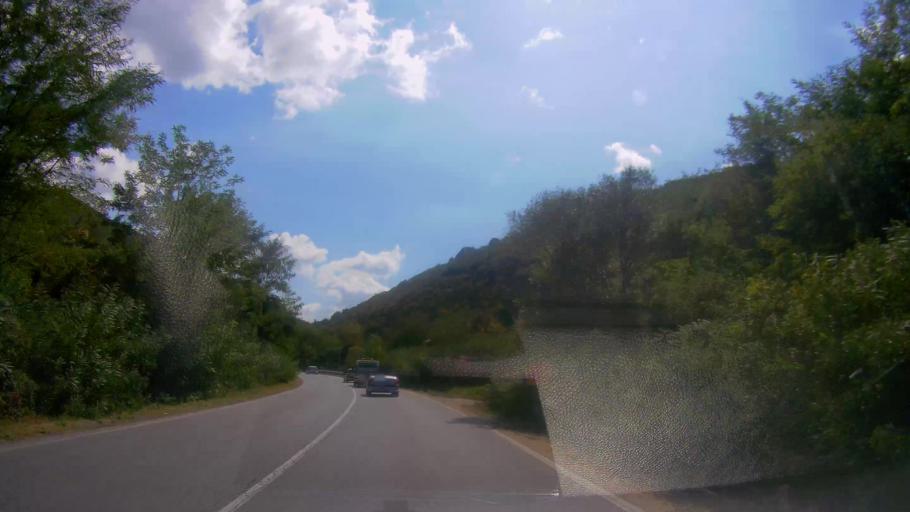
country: BG
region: Stara Zagora
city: Gurkovo
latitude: 42.7363
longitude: 25.7080
